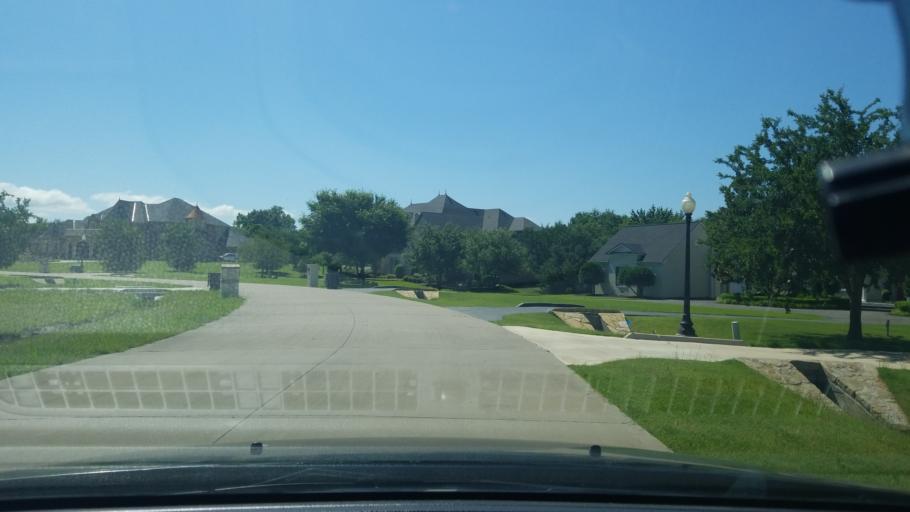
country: US
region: Texas
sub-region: Dallas County
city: Sunnyvale
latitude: 32.7970
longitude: -96.5678
